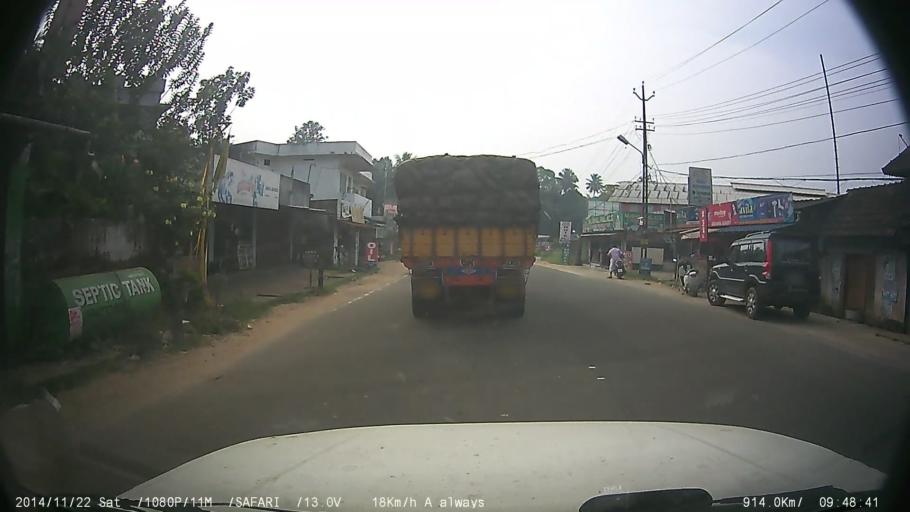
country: IN
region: Kerala
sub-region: Ernakulam
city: Perumpavur
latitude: 10.1267
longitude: 76.4732
